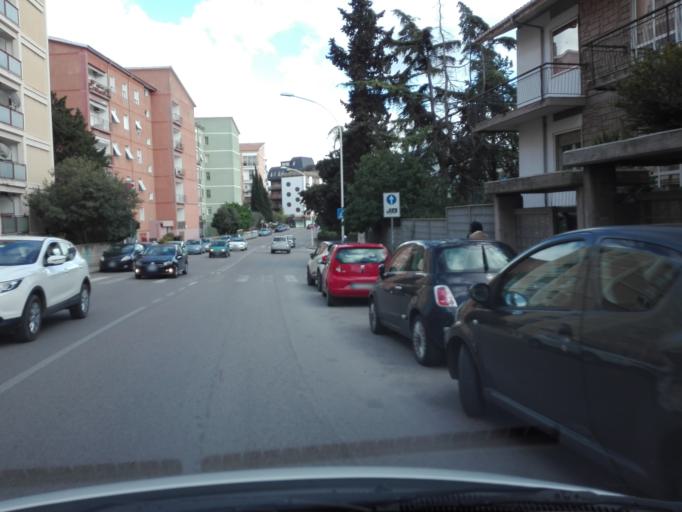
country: IT
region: Sardinia
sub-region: Provincia di Sassari
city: Sassari
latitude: 40.7220
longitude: 8.5771
